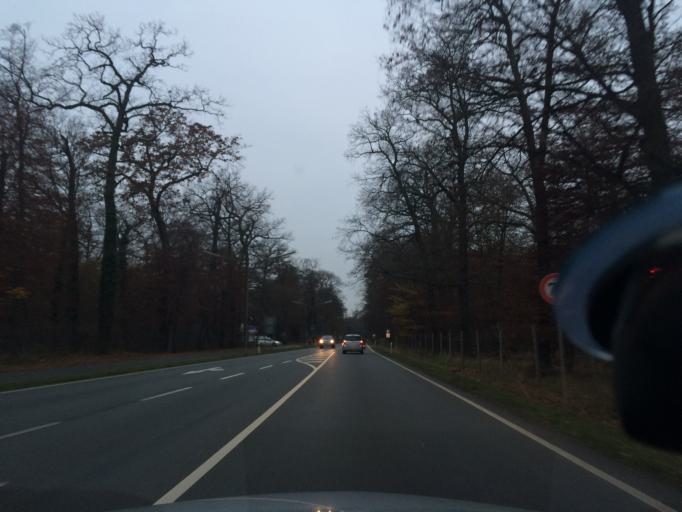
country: DE
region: Hesse
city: Morfelden-Walldorf
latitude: 49.9733
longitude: 8.5487
